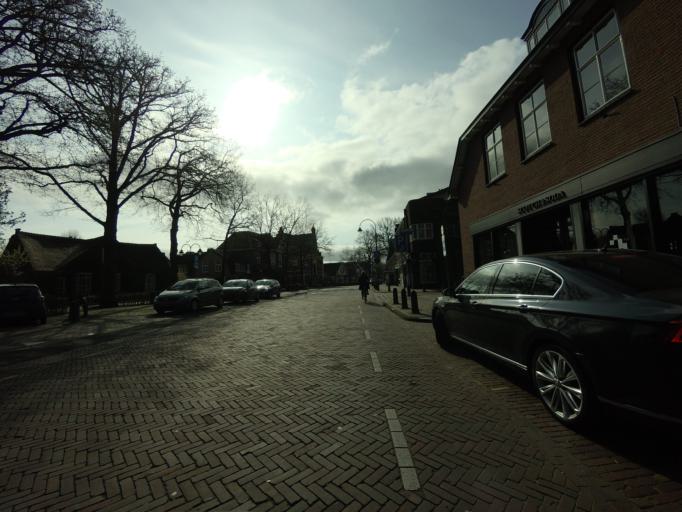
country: NL
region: North Holland
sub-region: Gemeente Laren
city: Laren
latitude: 52.2562
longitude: 5.2260
